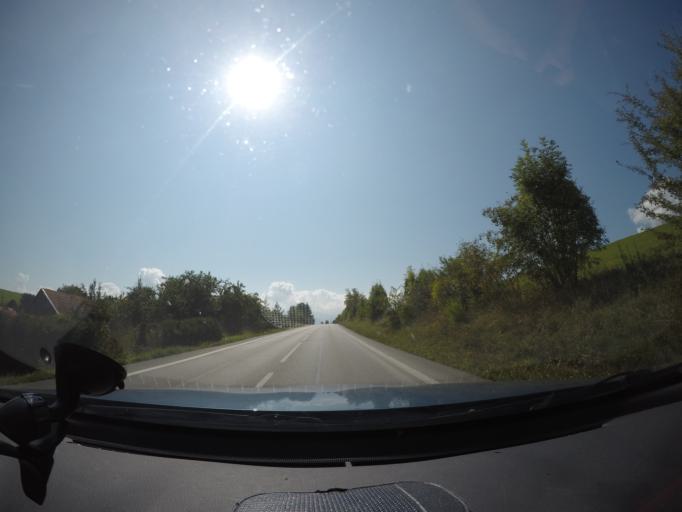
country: SK
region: Zilinsky
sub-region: Okres Liptovsky Mikulas
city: Liptovsky Mikulas
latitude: 49.1179
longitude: 19.5450
